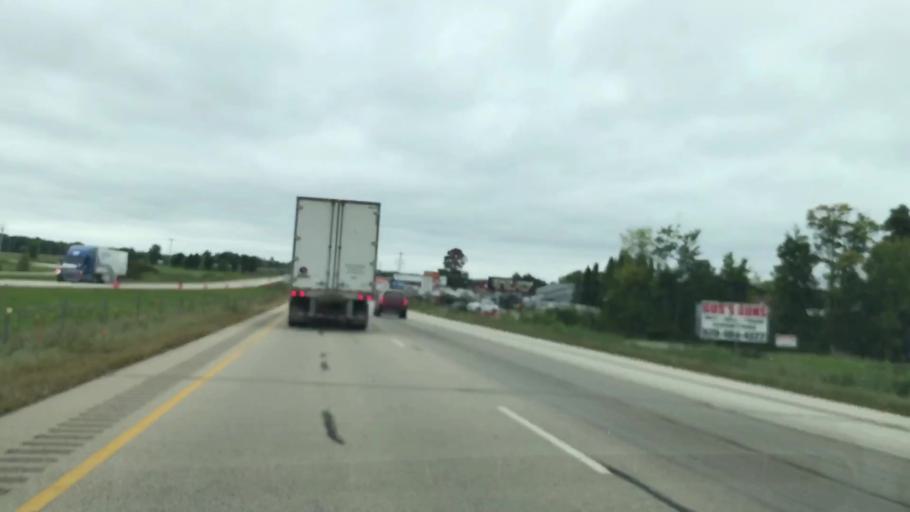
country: US
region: Wisconsin
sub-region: Brown County
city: Suamico
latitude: 44.6703
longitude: -88.0504
